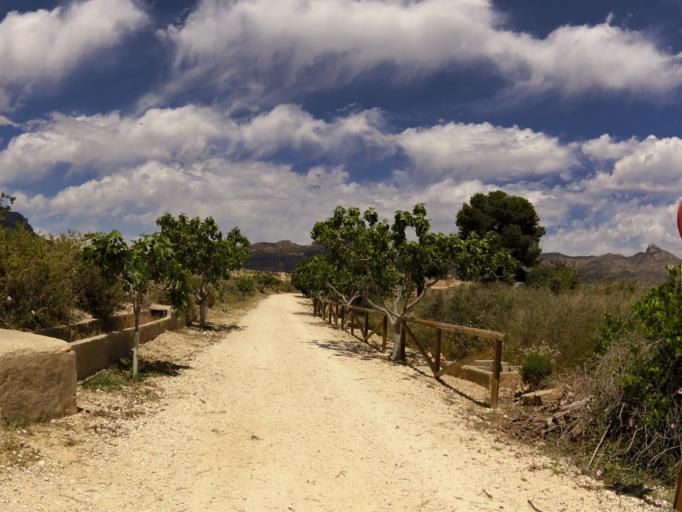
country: ES
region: Valencia
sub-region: Provincia de Alicante
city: Agost
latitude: 38.4461
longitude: -0.6669
